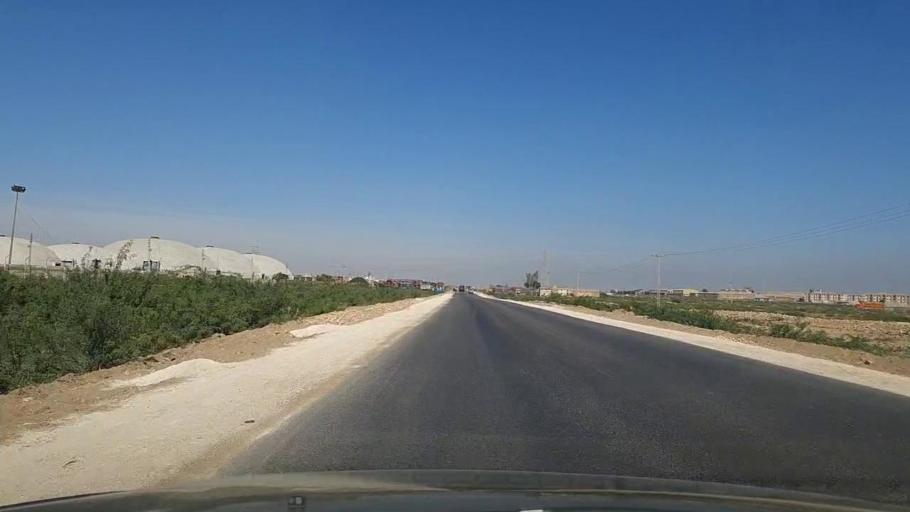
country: PK
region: Sindh
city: Kotri
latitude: 25.3286
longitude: 68.2406
